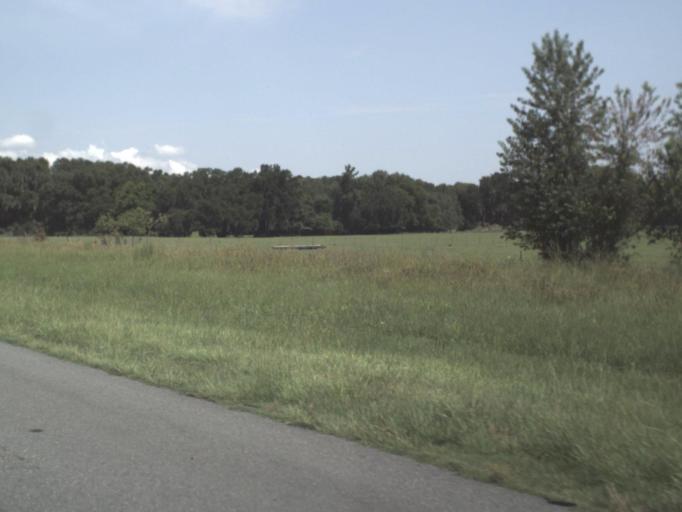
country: US
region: Florida
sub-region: Hamilton County
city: Jasper
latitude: 30.4830
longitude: -82.9945
